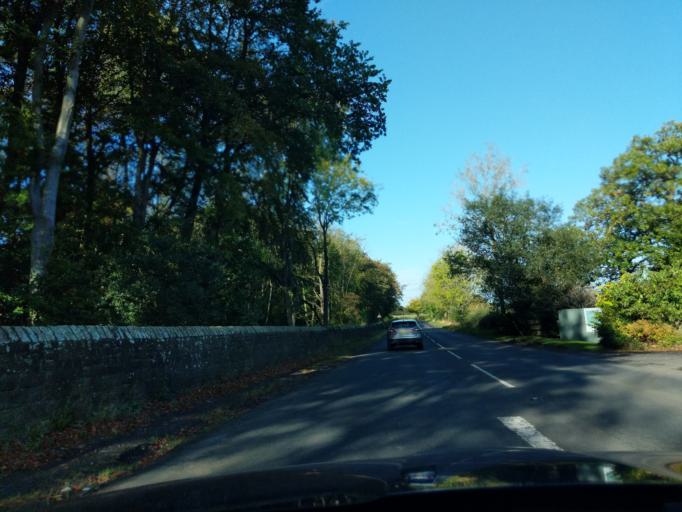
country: GB
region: England
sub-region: Northumberland
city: Stannington
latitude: 55.0863
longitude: -1.6520
